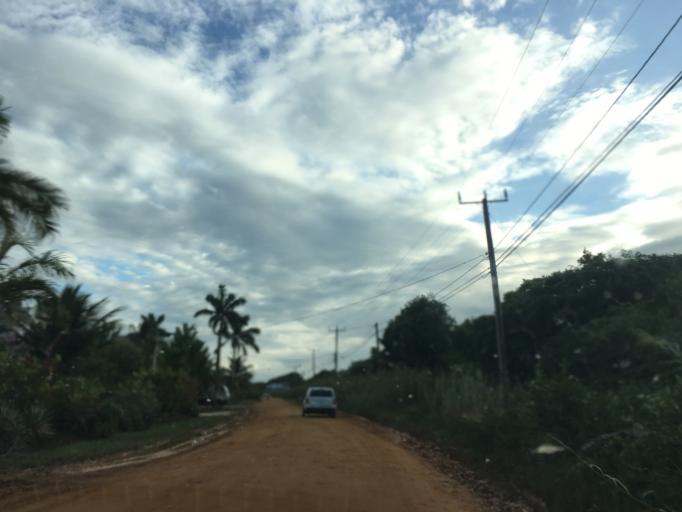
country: BZ
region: Stann Creek
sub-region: Dangriga
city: Dangriga
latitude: 16.8286
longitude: -88.2672
